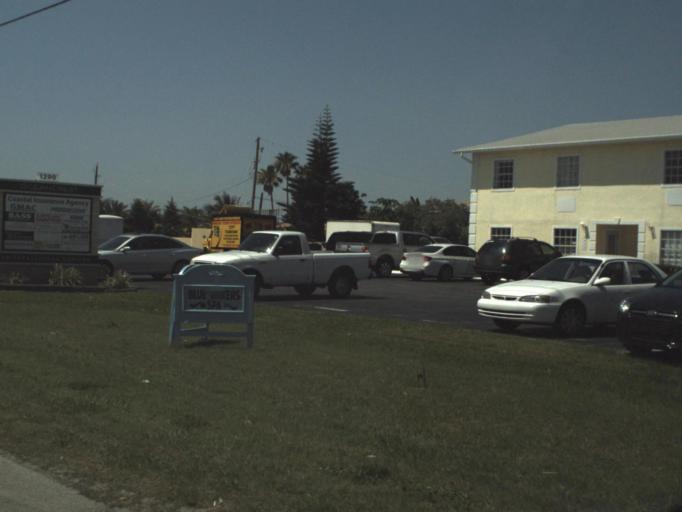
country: US
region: Florida
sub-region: Brevard County
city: Satellite Beach
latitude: 28.1771
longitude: -80.5908
